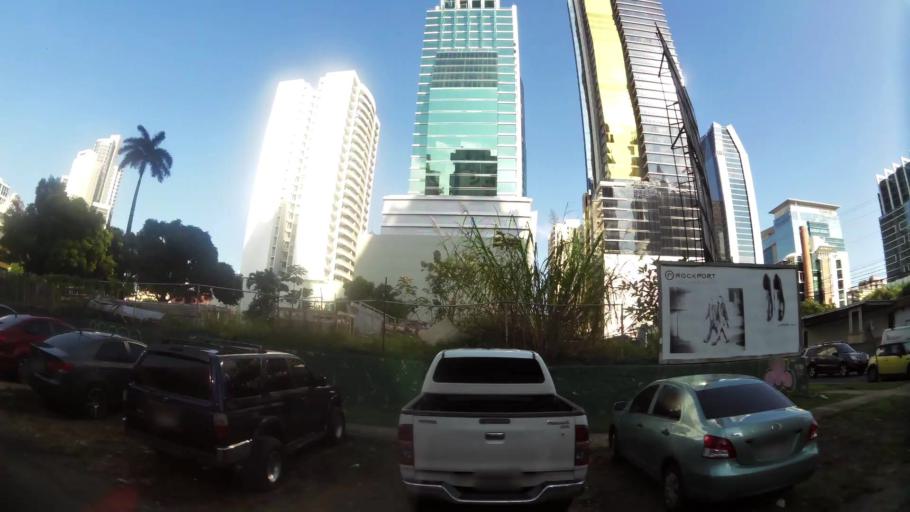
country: PA
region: Panama
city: Panama
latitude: 8.9838
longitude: -79.5208
